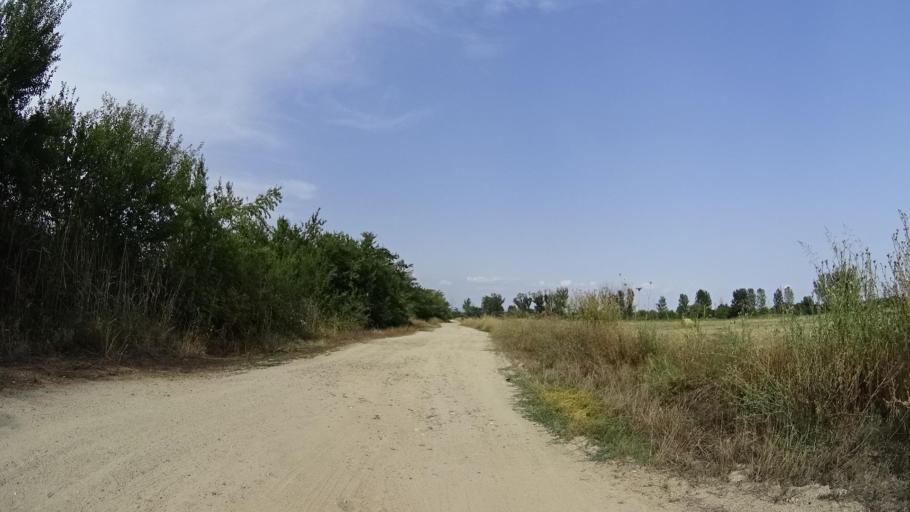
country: BG
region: Plovdiv
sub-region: Obshtina Kaloyanovo
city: Kaloyanovo
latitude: 42.2972
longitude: 24.7968
